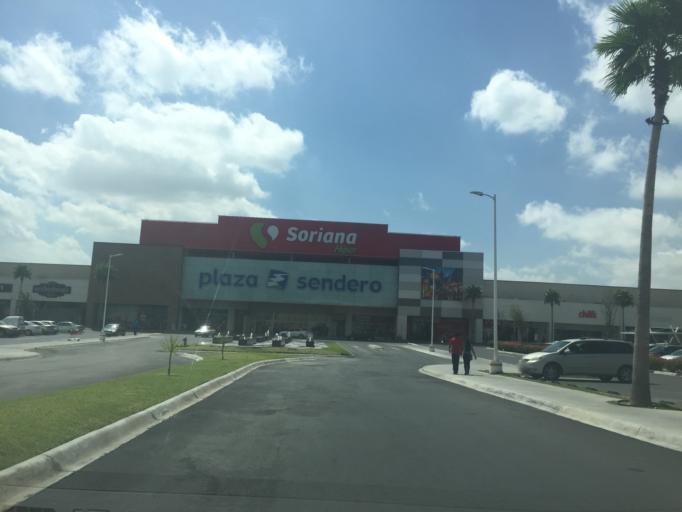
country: MX
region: Nuevo Leon
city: Apodaca
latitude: 25.7639
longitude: -100.1924
